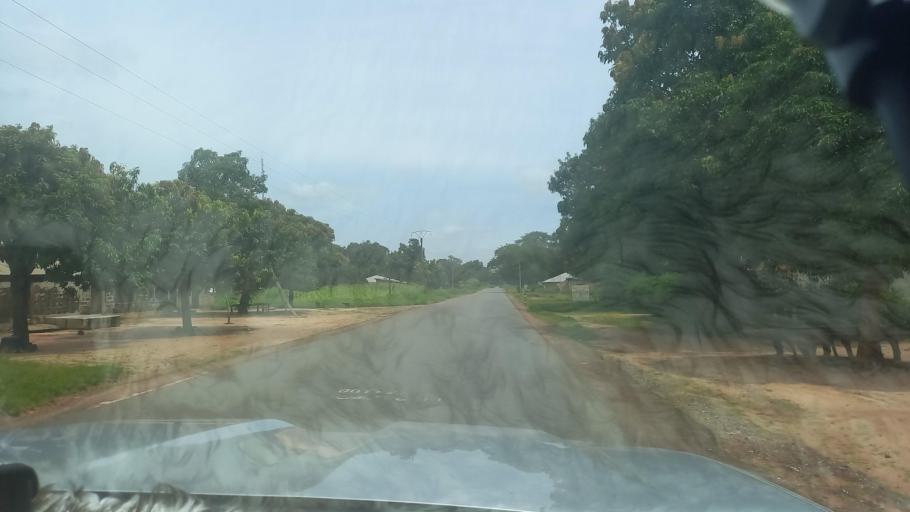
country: SN
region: Kolda
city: Marsassoum
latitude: 12.9642
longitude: -15.9741
